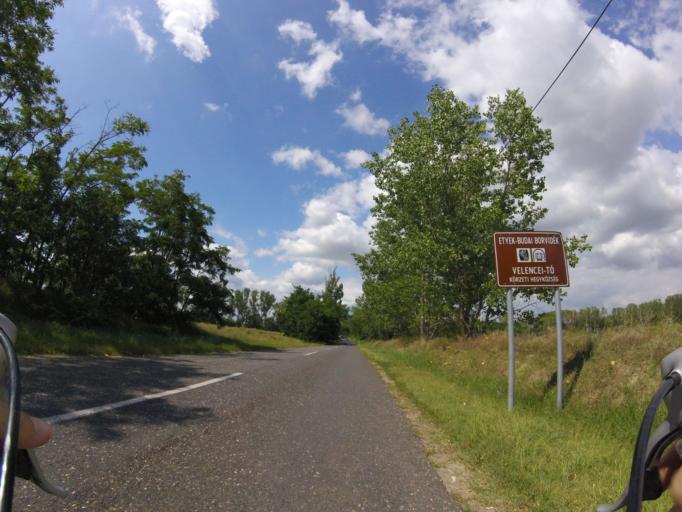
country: HU
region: Fejer
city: Seregelyes
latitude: 47.1278
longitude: 18.5767
